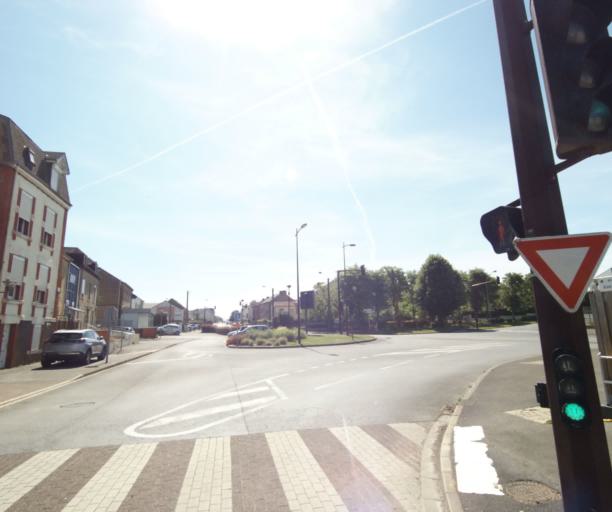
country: FR
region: Champagne-Ardenne
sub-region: Departement des Ardennes
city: Villers-Semeuse
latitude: 49.7431
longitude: 4.7395
